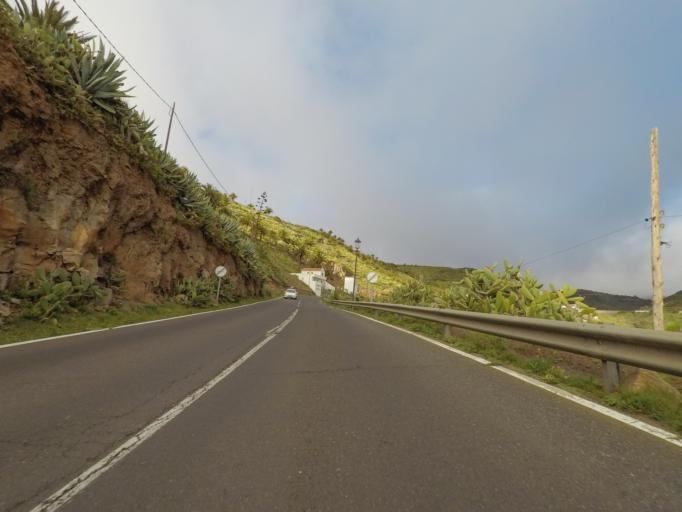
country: ES
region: Canary Islands
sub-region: Provincia de Santa Cruz de Tenerife
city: Vallehermosa
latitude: 28.1368
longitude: -17.3158
